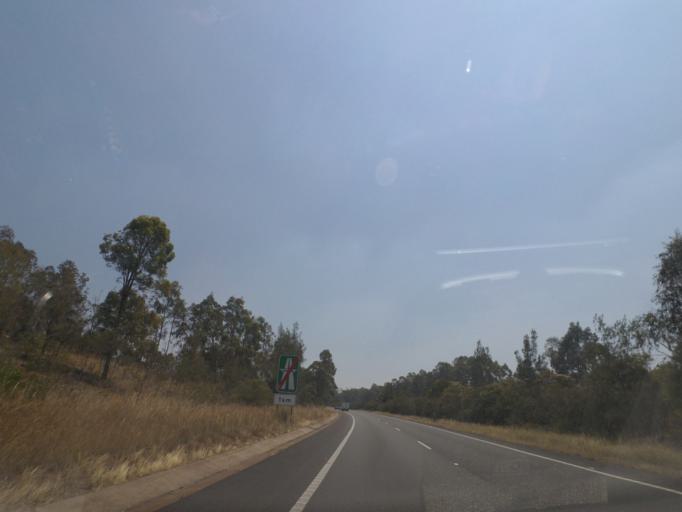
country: AU
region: New South Wales
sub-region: Newcastle
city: Beresfield
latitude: -32.8366
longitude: 151.6349
